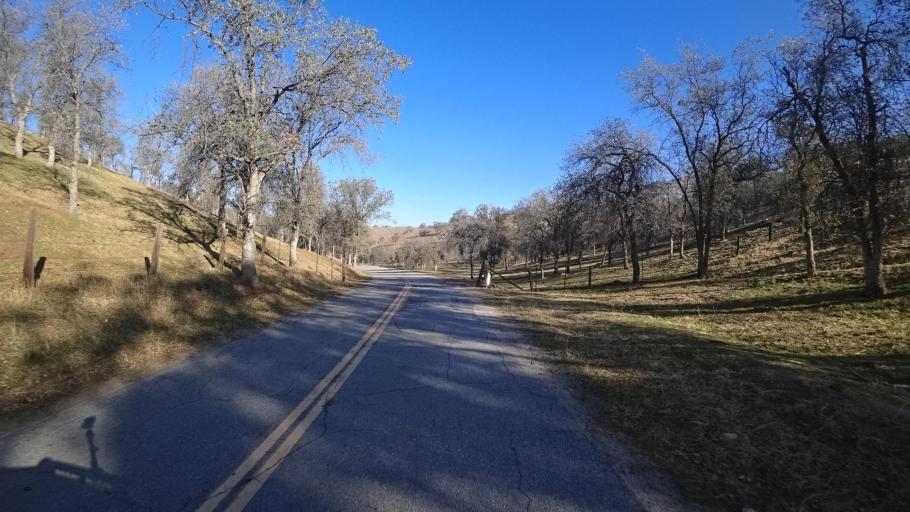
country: US
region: California
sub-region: Kern County
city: Alta Sierra
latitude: 35.7616
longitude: -118.8199
